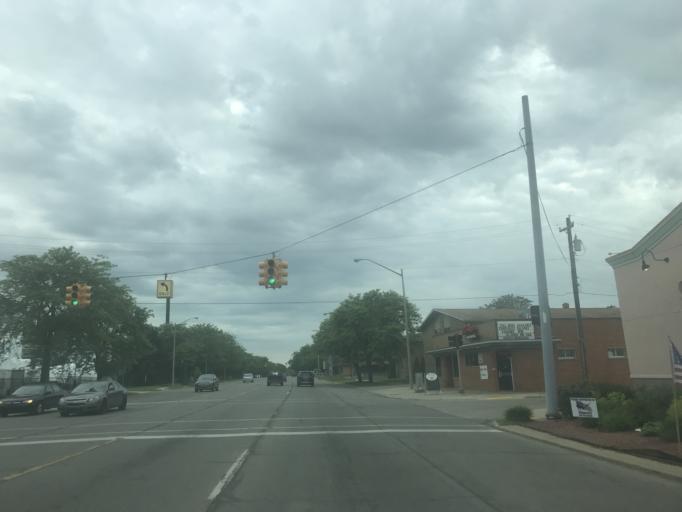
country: US
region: Michigan
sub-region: Wayne County
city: Wyandotte
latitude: 42.2266
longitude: -83.1500
